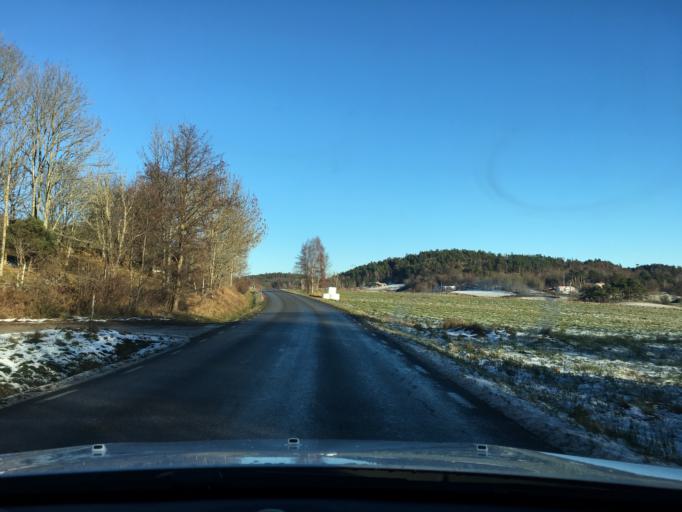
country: SE
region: Vaestra Goetaland
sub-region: Tjorns Kommun
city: Myggenas
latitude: 58.0363
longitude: 11.6702
